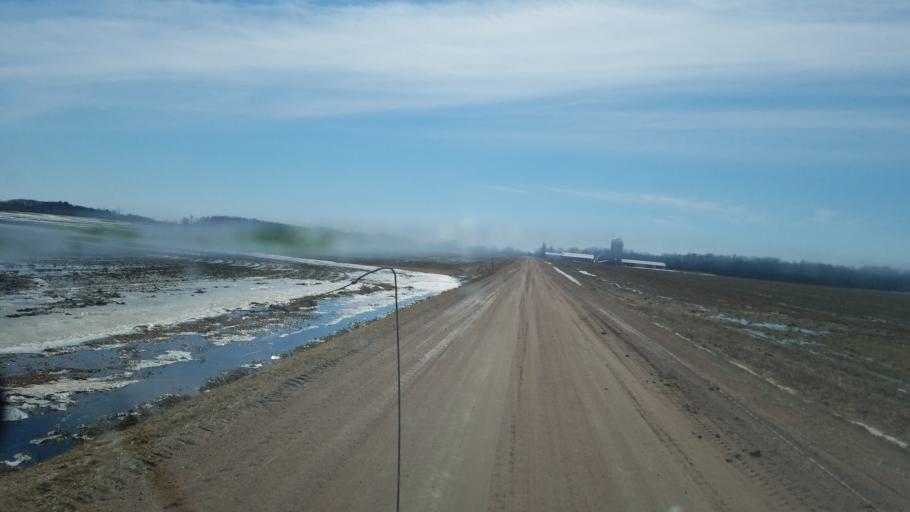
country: US
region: Wisconsin
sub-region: Clark County
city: Loyal
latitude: 44.6391
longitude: -90.4075
